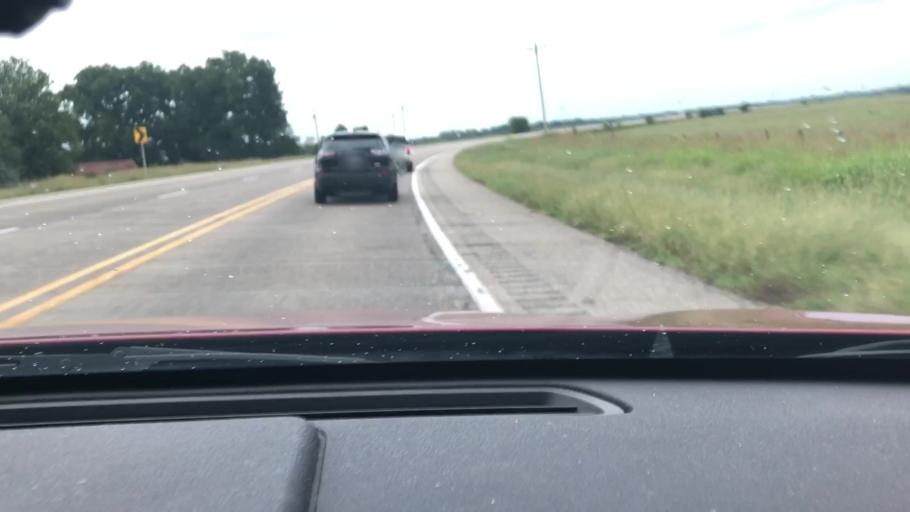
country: US
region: Arkansas
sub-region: Lafayette County
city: Lewisville
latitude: 33.3930
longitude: -93.7382
